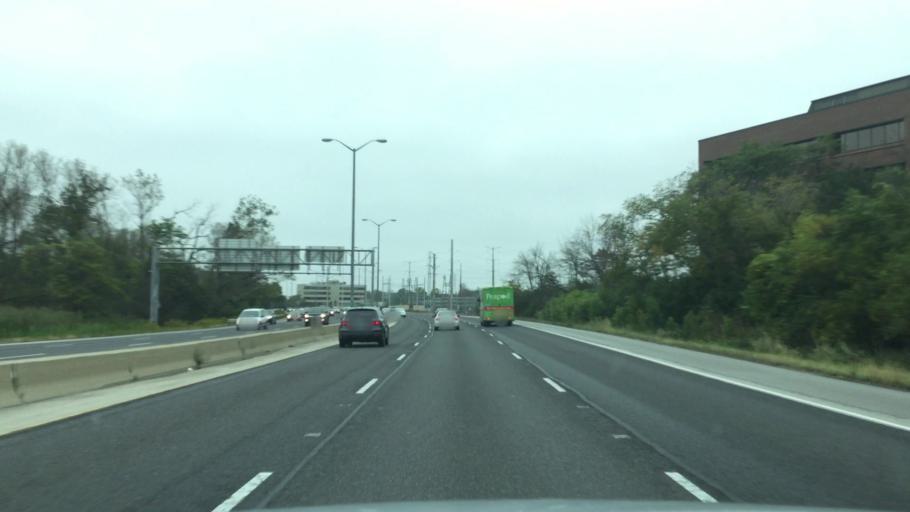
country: US
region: Illinois
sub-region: Cook County
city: Glencoe
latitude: 42.1307
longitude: -87.7854
